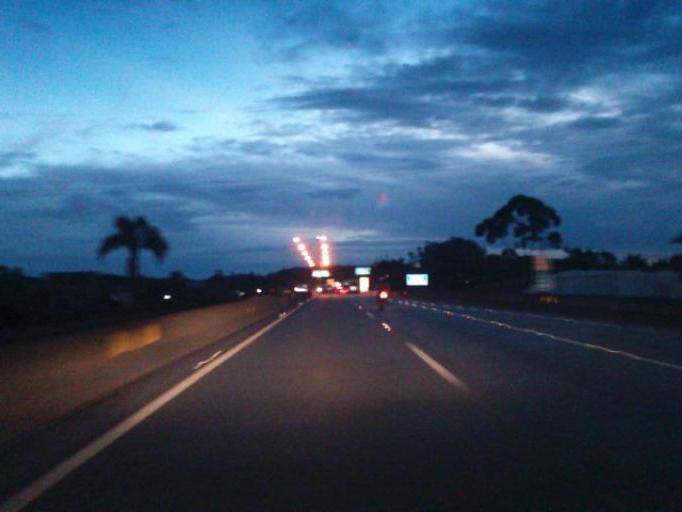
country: BR
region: Santa Catarina
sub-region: Barra Velha
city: Barra Velha
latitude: -26.5970
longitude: -48.7233
